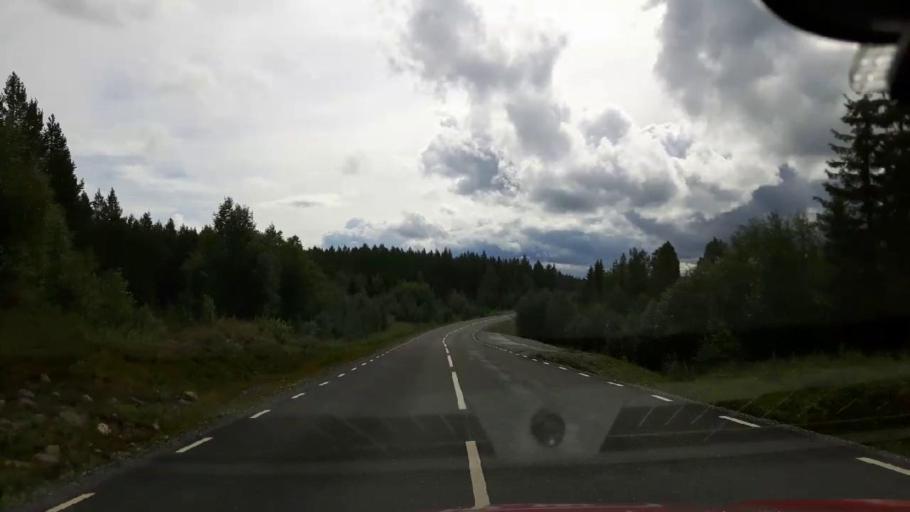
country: NO
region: Nord-Trondelag
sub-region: Lierne
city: Sandvika
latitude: 64.6090
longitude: 14.1193
